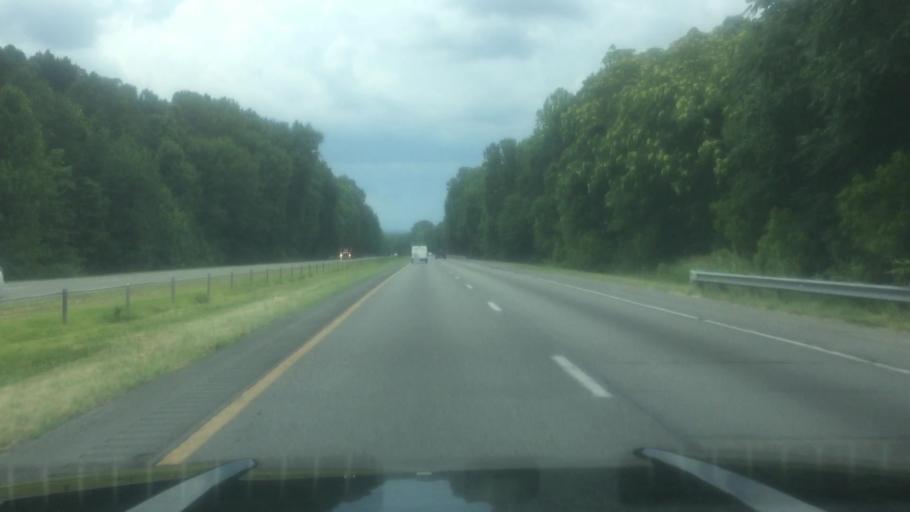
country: US
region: North Carolina
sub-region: Surry County
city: Pilot Mountain
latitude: 36.3502
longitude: -80.4668
